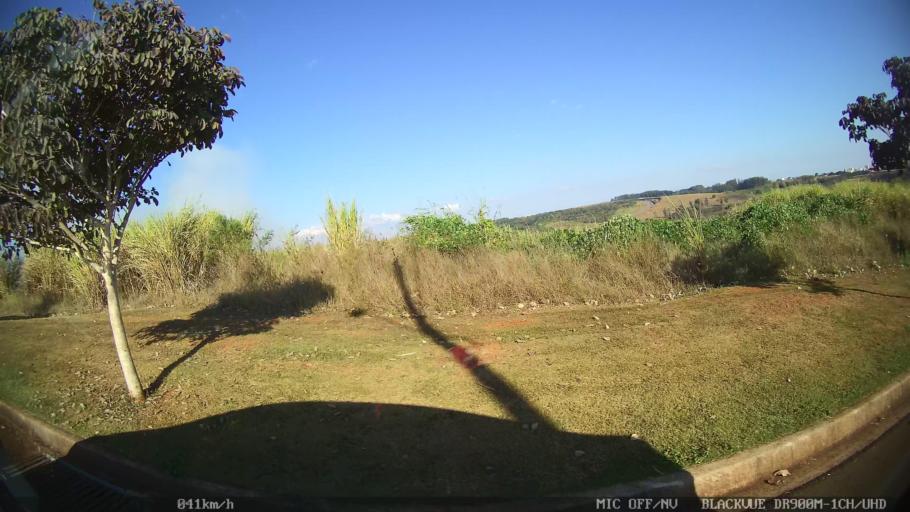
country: BR
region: Sao Paulo
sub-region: Piracicaba
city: Piracicaba
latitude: -22.6918
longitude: -47.6146
